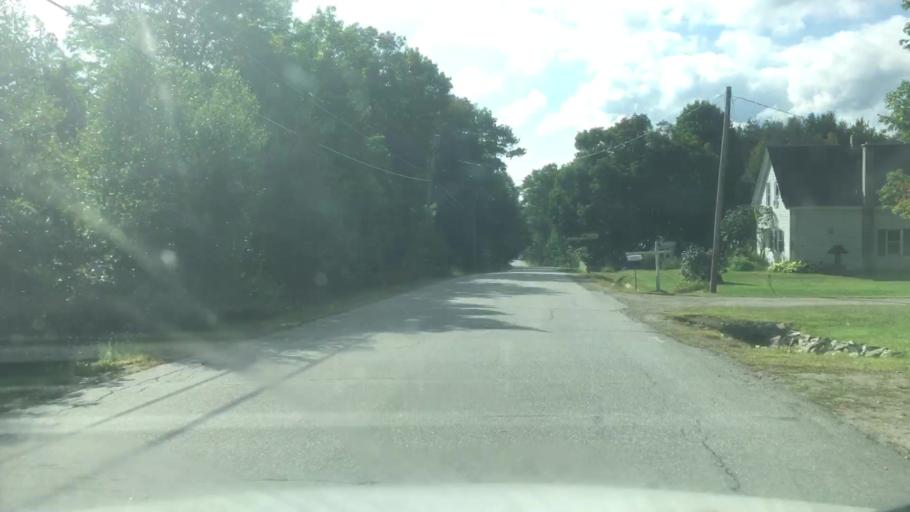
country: US
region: Maine
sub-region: Kennebec County
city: Gardiner
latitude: 44.1769
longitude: -69.8228
